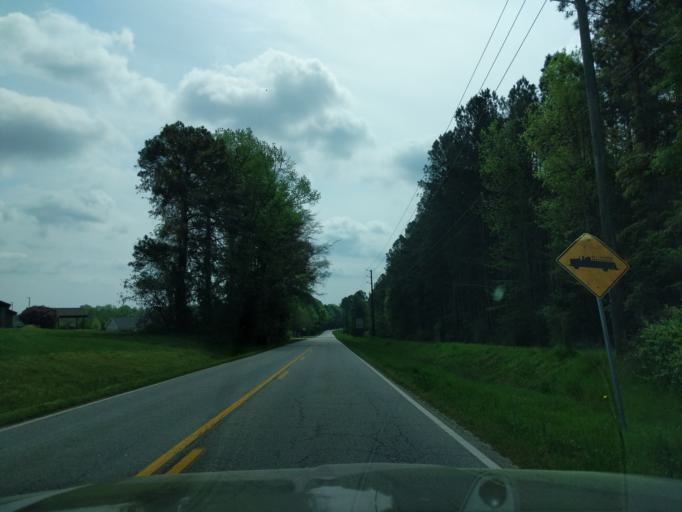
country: US
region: Georgia
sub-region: Columbia County
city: Appling
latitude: 33.6103
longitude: -82.3262
